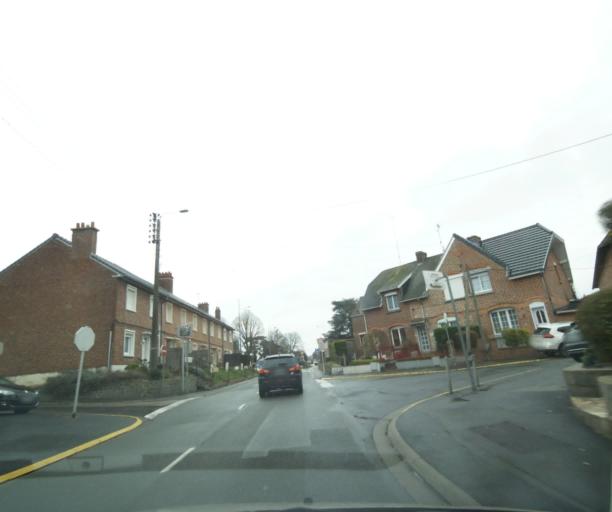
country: FR
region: Nord-Pas-de-Calais
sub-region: Departement du Nord
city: Prouvy
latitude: 50.3209
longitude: 3.4504
